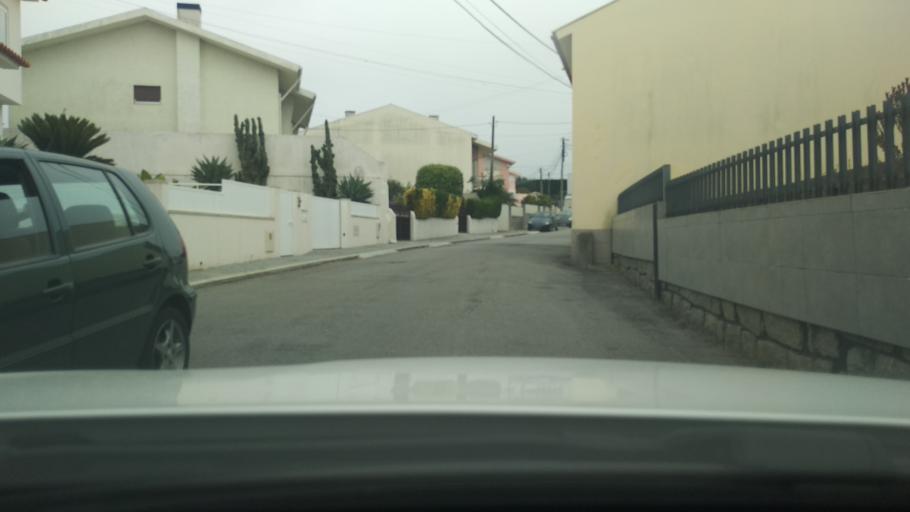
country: PT
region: Aveiro
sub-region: Espinho
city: Silvalde
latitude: 40.9963
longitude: -8.6307
